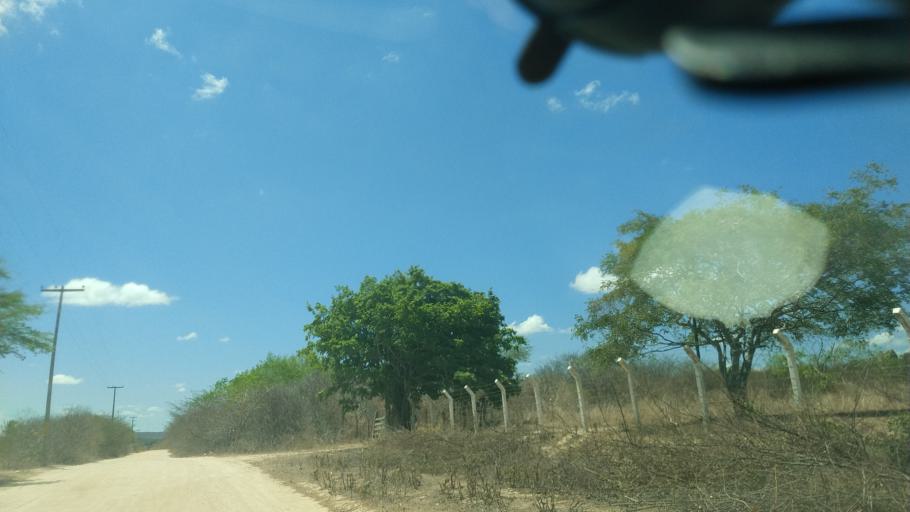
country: BR
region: Rio Grande do Norte
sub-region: Cerro Cora
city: Cerro Cora
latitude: -6.0255
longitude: -36.3353
